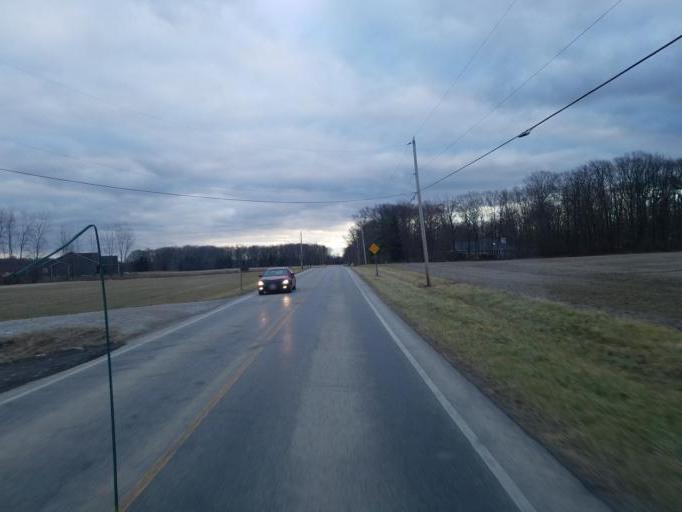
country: US
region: Ohio
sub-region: Delaware County
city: Delaware
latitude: 40.3371
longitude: -83.1310
